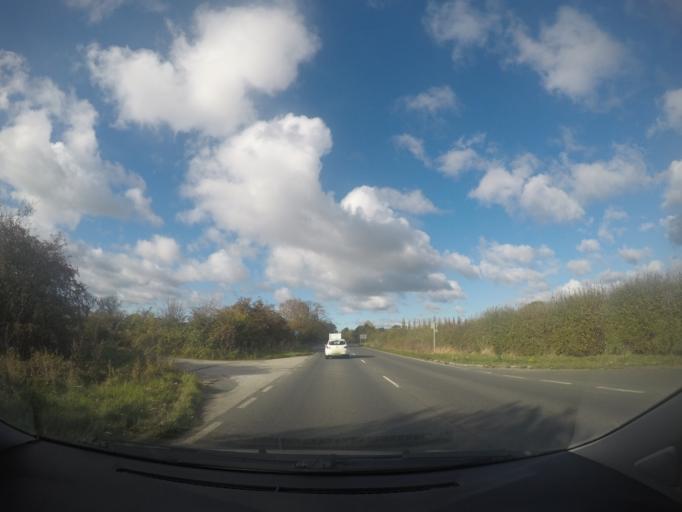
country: GB
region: England
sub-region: City of York
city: Nether Poppleton
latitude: 53.9767
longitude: -1.1815
